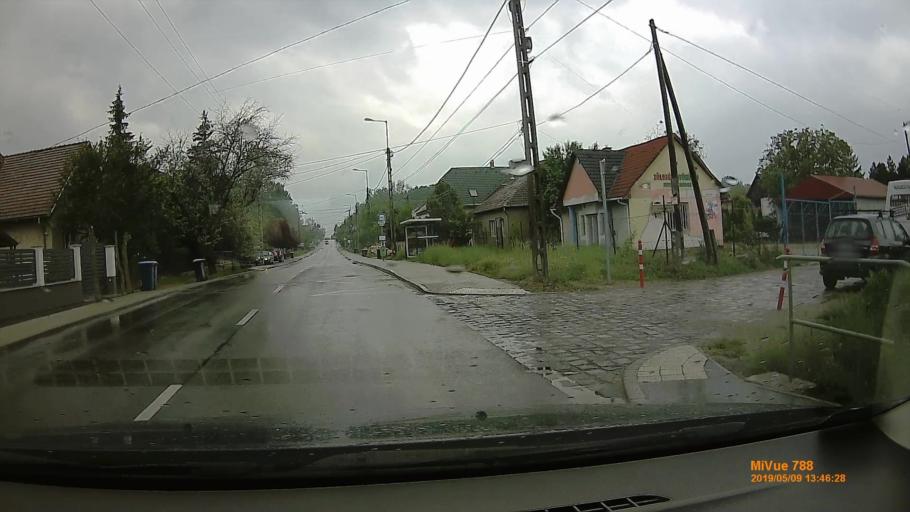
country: HU
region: Budapest
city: Budapest XVI. keruelet
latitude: 47.5303
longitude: 19.1876
